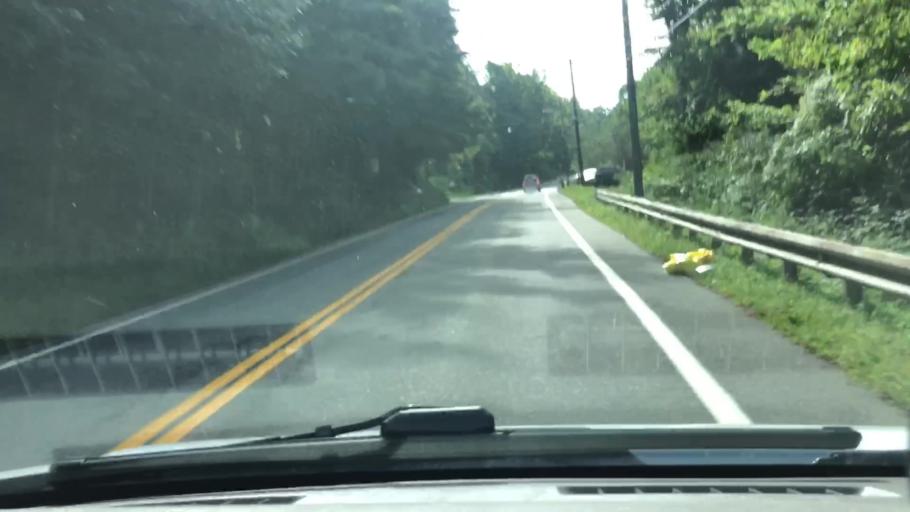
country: US
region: Massachusetts
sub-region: Berkshire County
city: North Adams
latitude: 42.6936
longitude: -73.0869
